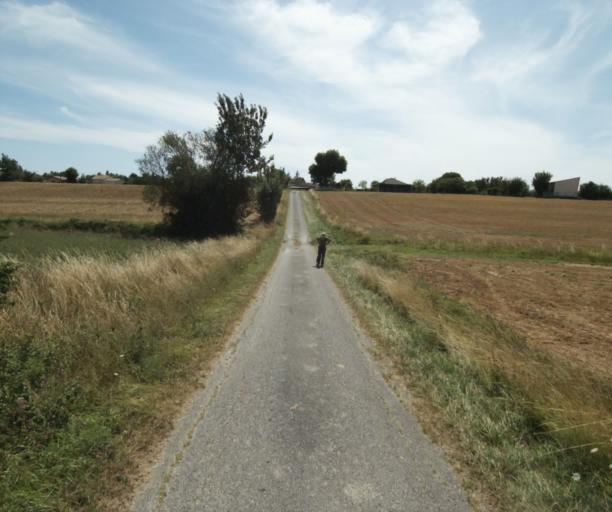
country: FR
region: Midi-Pyrenees
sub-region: Departement du Tarn
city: Puylaurens
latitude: 43.5365
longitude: 2.0168
